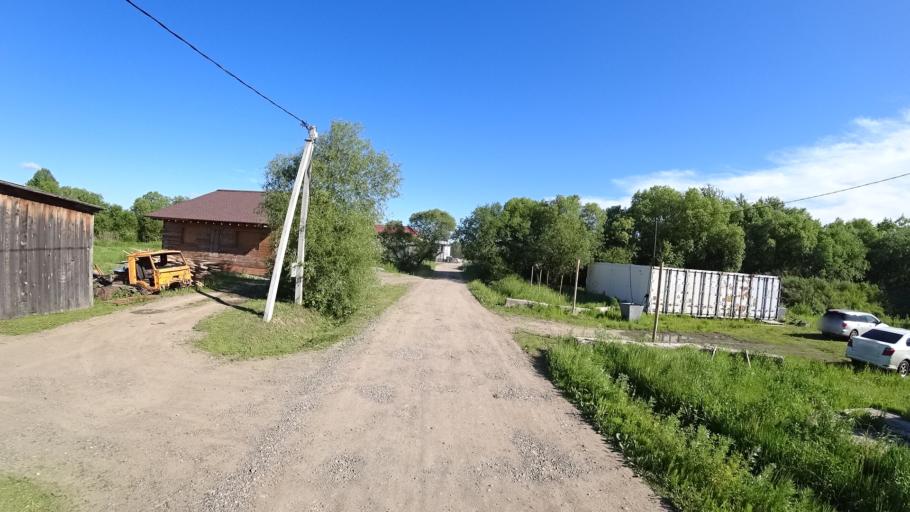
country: RU
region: Khabarovsk Krai
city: Khor
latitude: 47.8928
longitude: 134.9950
